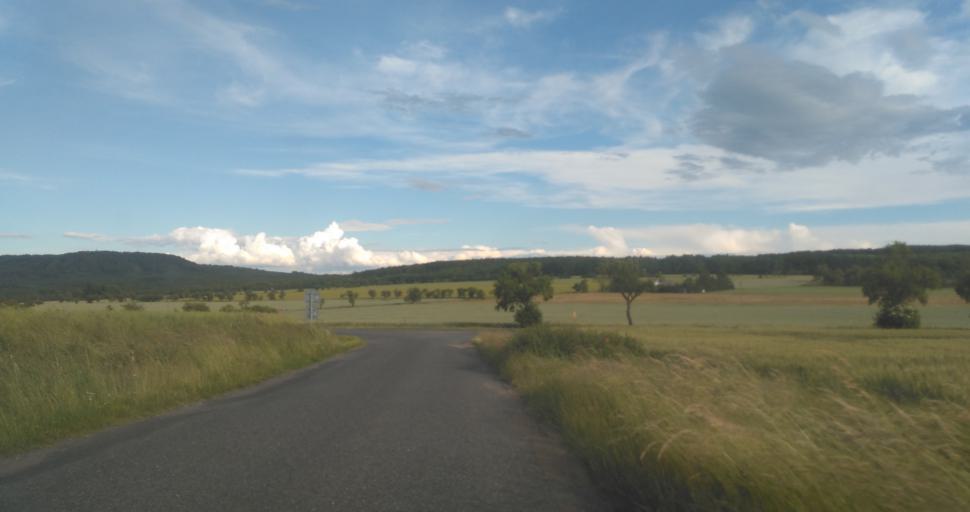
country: CZ
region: Central Bohemia
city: Roztoky
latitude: 49.9788
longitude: 13.8811
